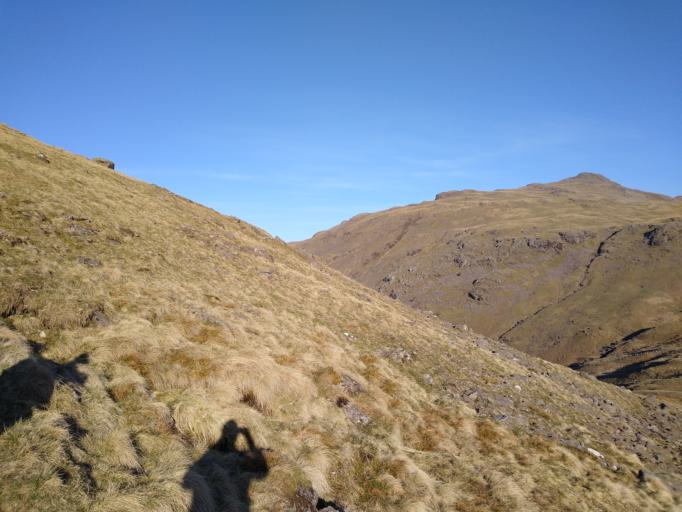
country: GB
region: England
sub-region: Cumbria
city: Ambleside
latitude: 54.4131
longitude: -3.1159
